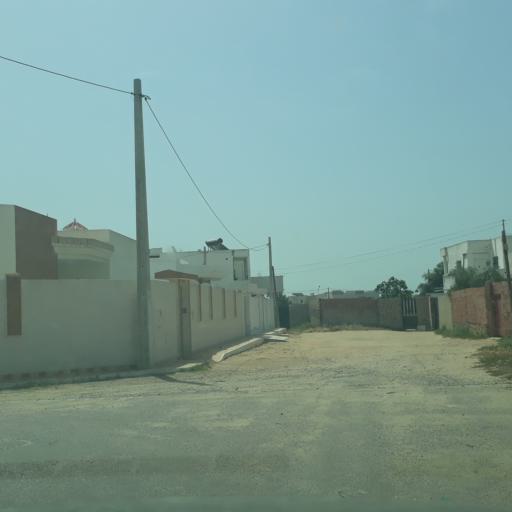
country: TN
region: Safaqis
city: Al Qarmadah
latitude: 34.7977
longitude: 10.7661
